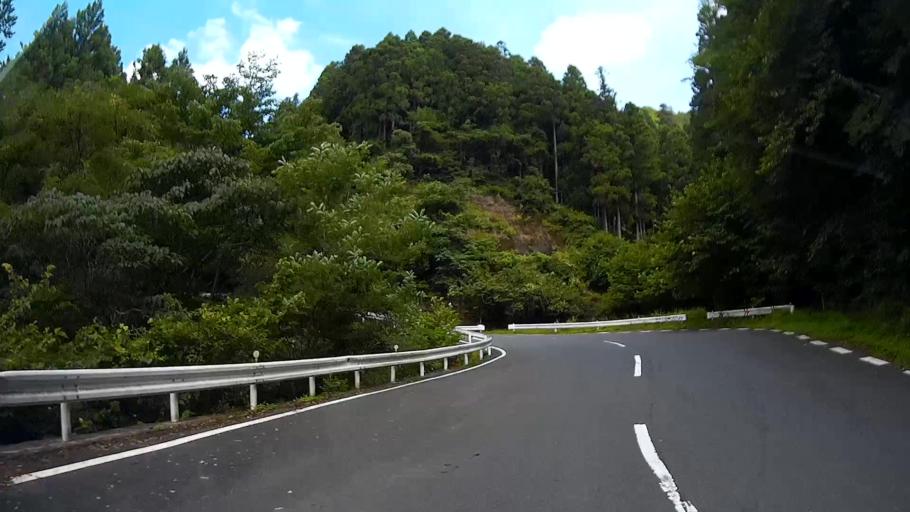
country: JP
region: Saitama
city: Chichibu
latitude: 35.9248
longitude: 139.1519
